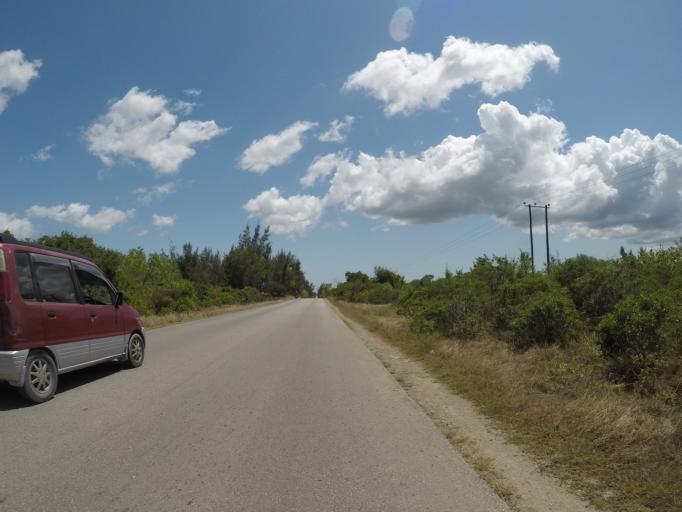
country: TZ
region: Zanzibar Central/South
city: Nganane
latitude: -6.2684
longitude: 39.5190
